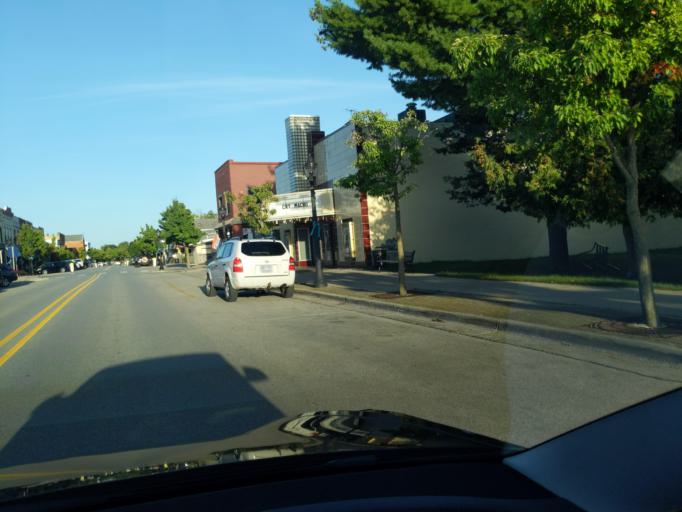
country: US
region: Michigan
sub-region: Antrim County
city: Elk Rapids
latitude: 44.8979
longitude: -85.4151
